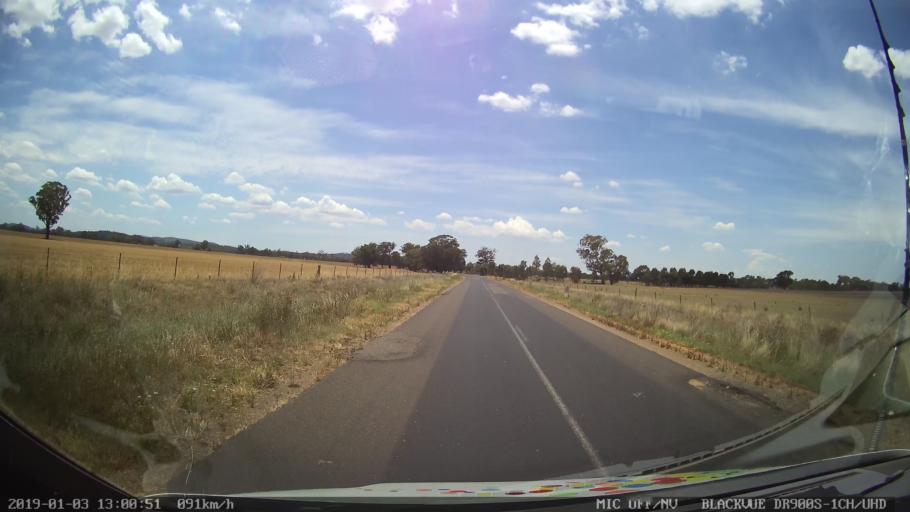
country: AU
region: New South Wales
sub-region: Cabonne
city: Canowindra
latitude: -33.6286
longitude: 148.4101
